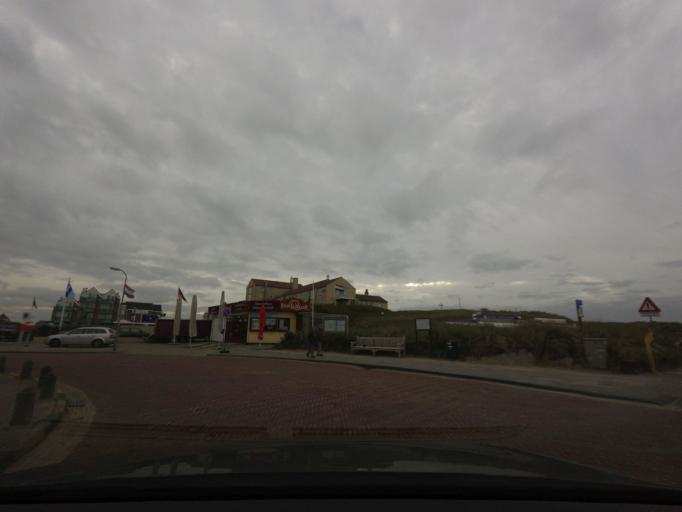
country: NL
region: North Holland
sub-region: Gemeente Bergen
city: Egmond aan Zee
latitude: 52.6604
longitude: 4.6298
